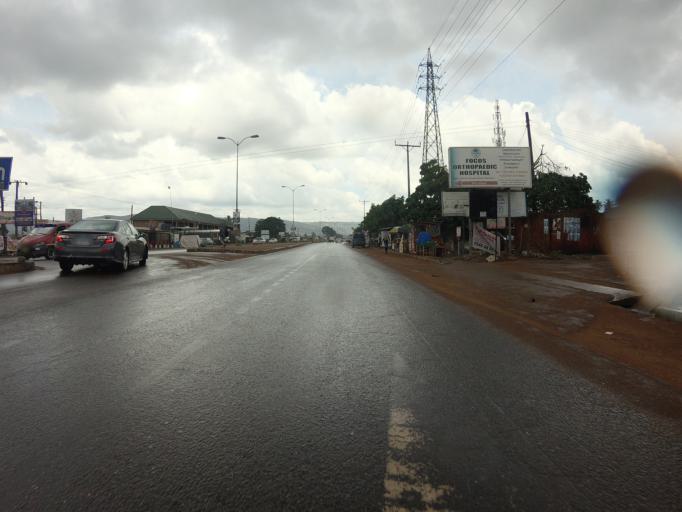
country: GH
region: Greater Accra
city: Medina Estates
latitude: 5.7445
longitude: -0.1770
